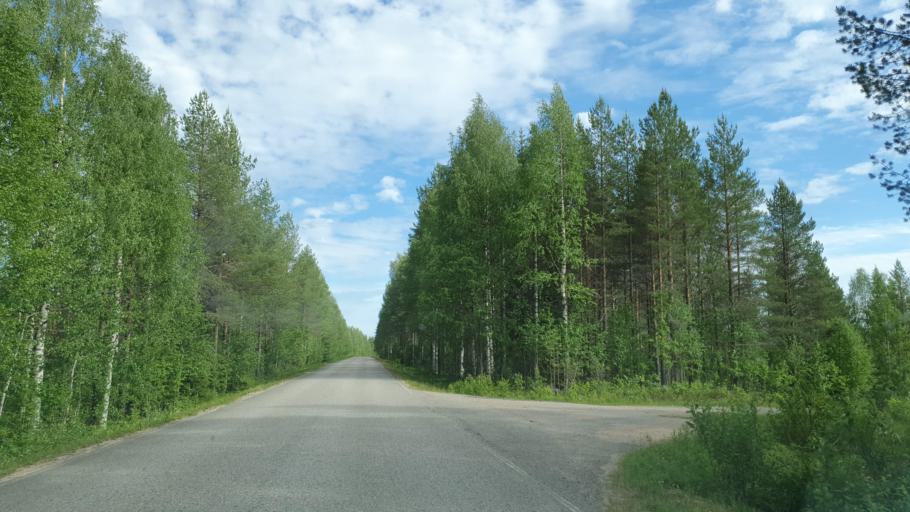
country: FI
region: Kainuu
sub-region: Kehys-Kainuu
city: Kuhmo
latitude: 64.5284
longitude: 29.3645
